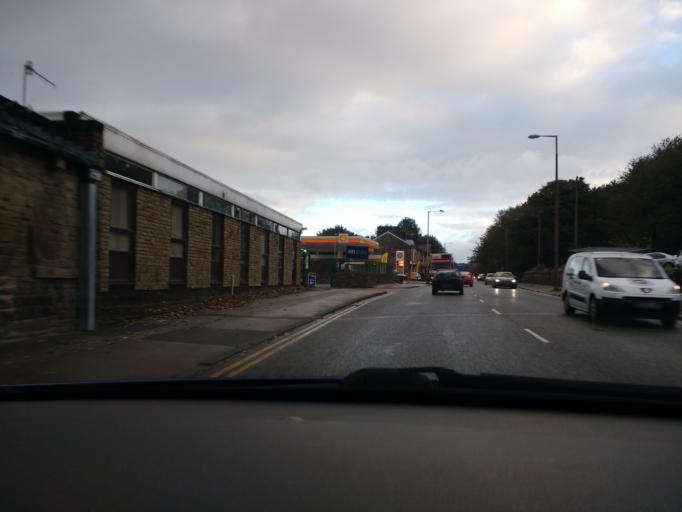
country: GB
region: England
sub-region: Lancashire
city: Bolton le Sands
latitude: 54.0639
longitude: -2.7873
